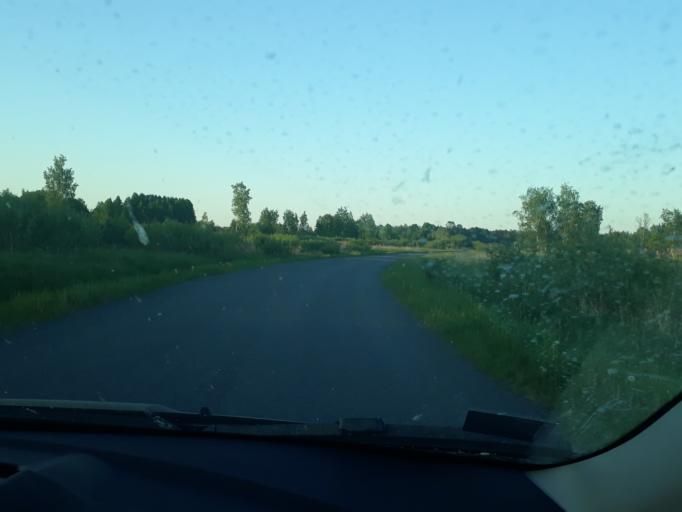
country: EE
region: Paernumaa
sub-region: Vaendra vald (alev)
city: Vandra
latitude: 58.5689
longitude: 24.9844
